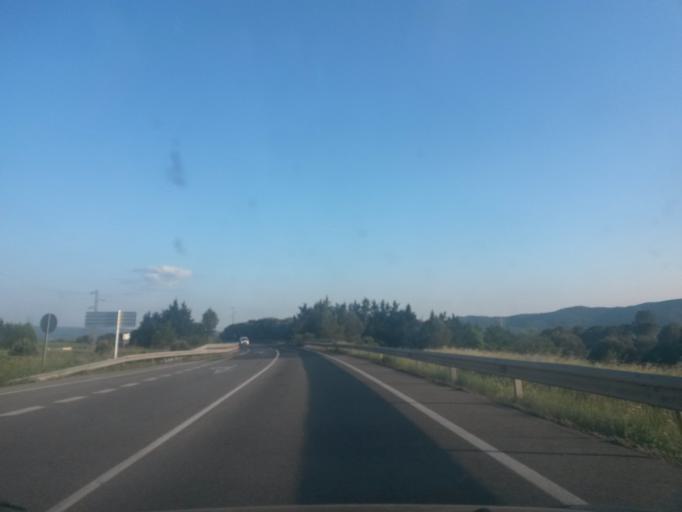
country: ES
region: Catalonia
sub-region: Provincia de Girona
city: Banyoles
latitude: 42.1321
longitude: 2.7737
